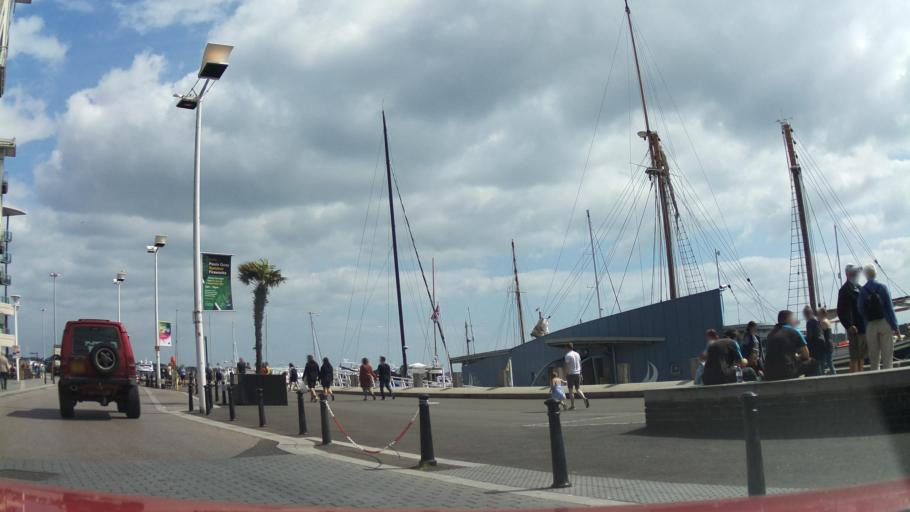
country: GB
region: England
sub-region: Poole
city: Poole
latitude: 50.7120
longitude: -1.9853
